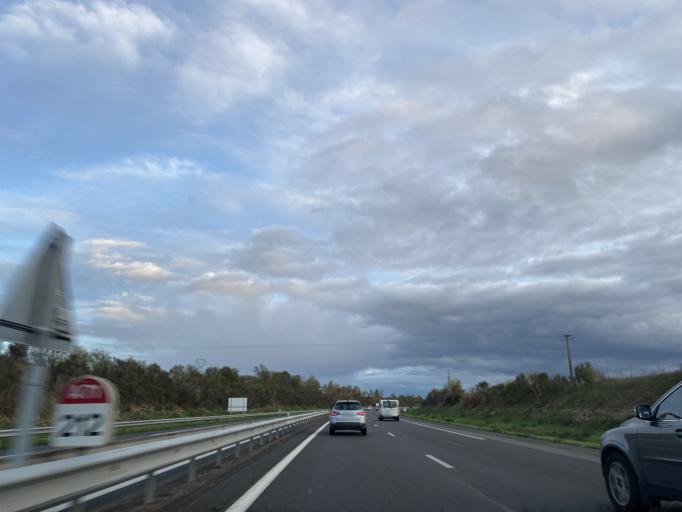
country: FR
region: Centre
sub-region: Departement du Cher
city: Trouy
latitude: 47.0358
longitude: 2.3669
